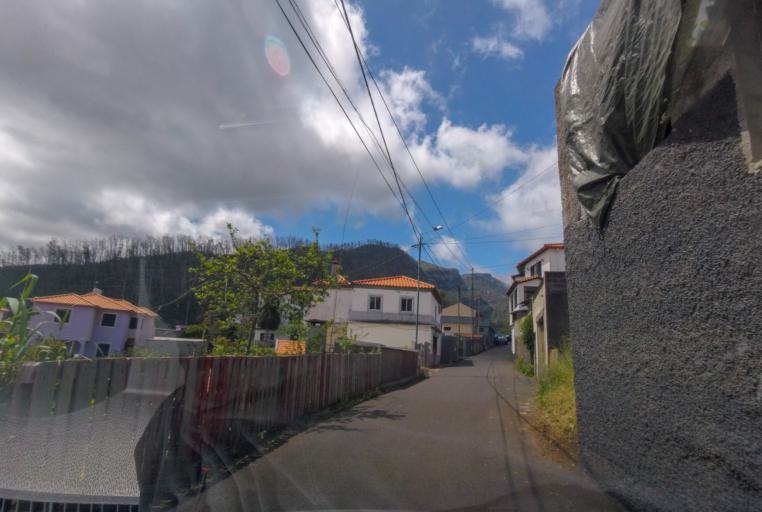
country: PT
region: Madeira
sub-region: Funchal
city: Nossa Senhora do Monte
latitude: 32.6817
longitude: -16.9127
